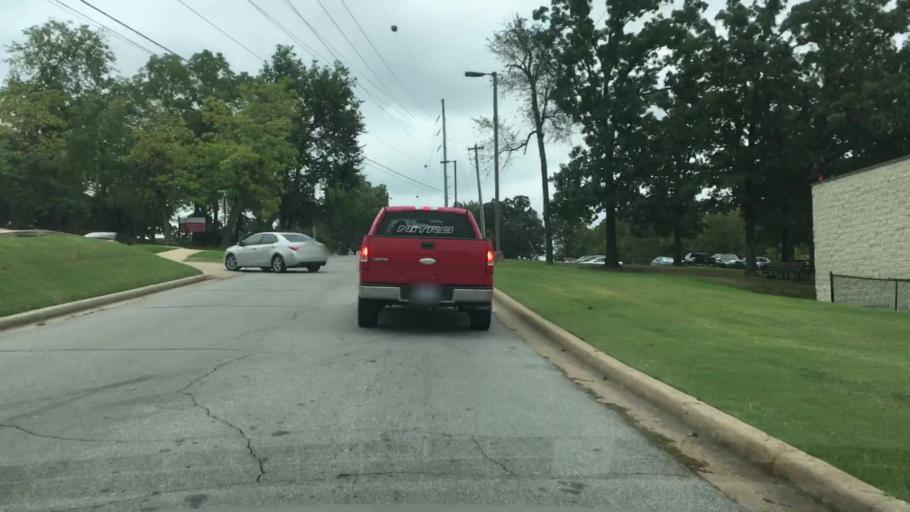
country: US
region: Oklahoma
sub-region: Cherokee County
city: Tahlequah
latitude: 35.9144
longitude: -94.9490
